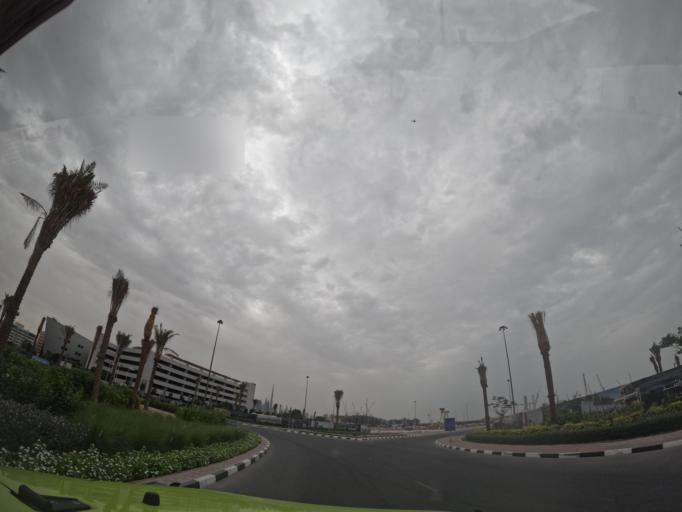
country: AE
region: Ash Shariqah
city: Sharjah
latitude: 25.2578
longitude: 55.2824
